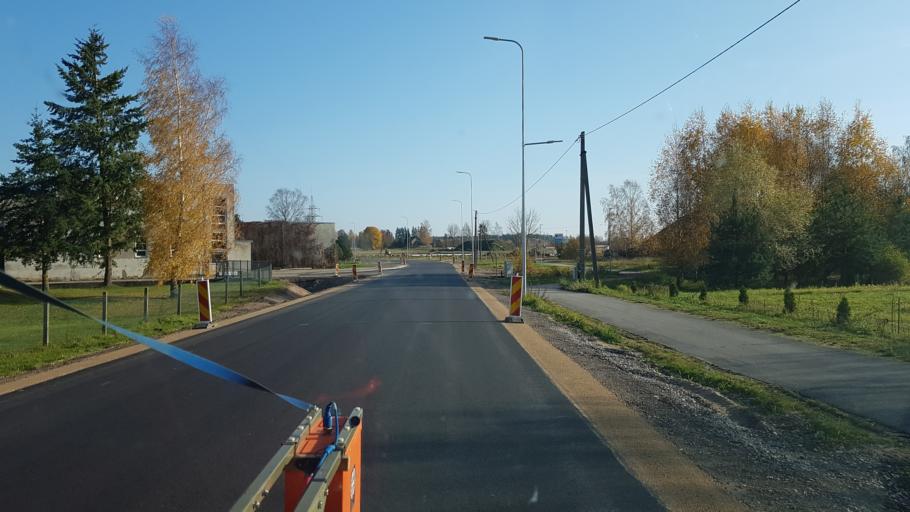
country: EE
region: Vorumaa
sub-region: Antsla vald
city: Vana-Antsla
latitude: 57.8409
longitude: 26.4803
